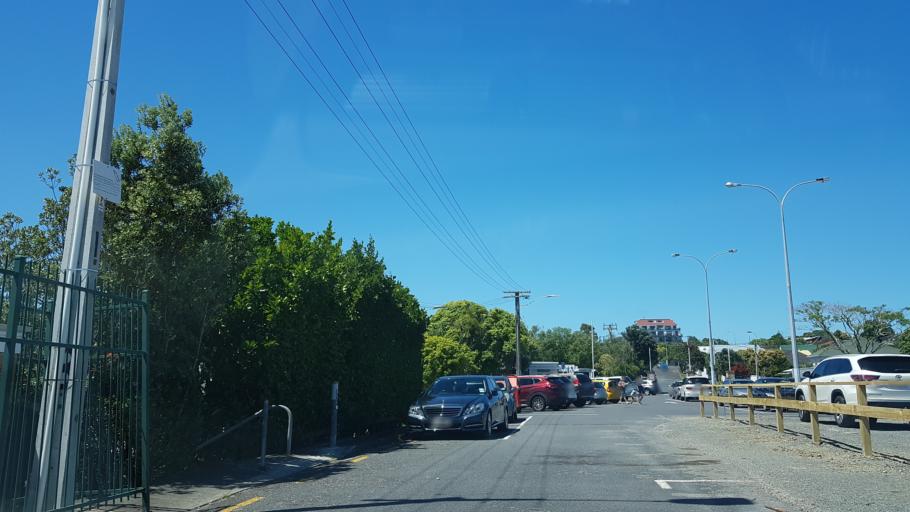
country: NZ
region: Auckland
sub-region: Auckland
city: North Shore
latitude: -36.8077
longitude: 174.7214
